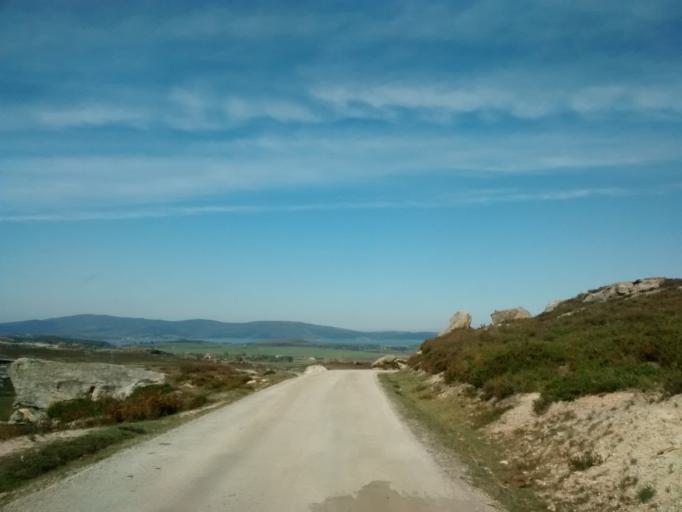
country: ES
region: Castille and Leon
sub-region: Provincia de Burgos
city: Arija
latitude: 42.9331
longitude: -3.9548
